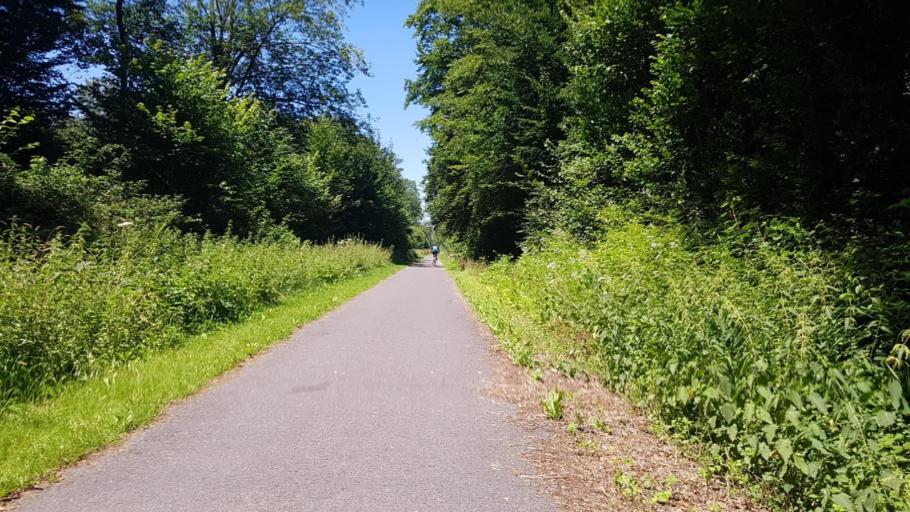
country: BE
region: Wallonia
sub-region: Province du Hainaut
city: Beaumont
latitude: 50.1682
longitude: 4.2423
